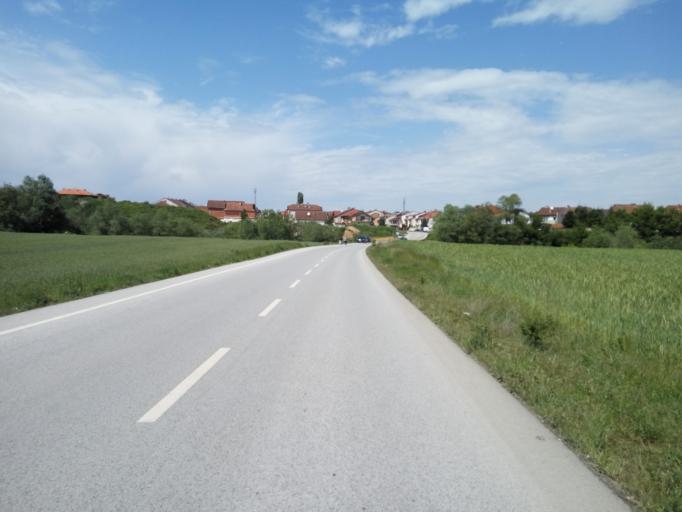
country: XK
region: Gjakova
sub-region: Komuna e Gjakoves
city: Gjakove
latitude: 42.3642
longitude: 20.4355
